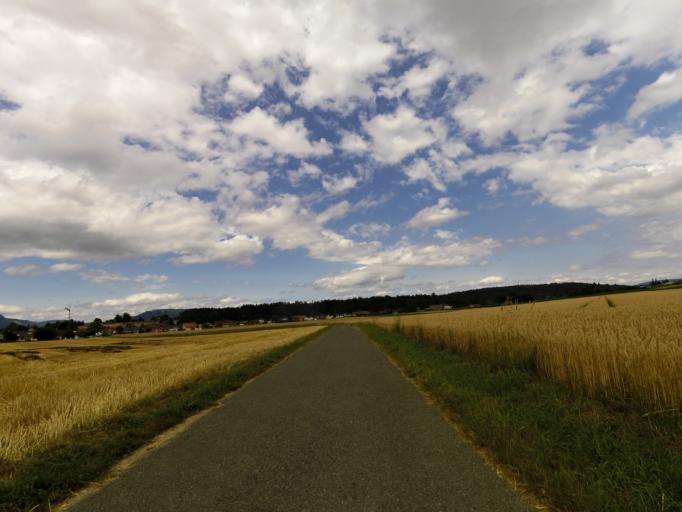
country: CH
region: Bern
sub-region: Oberaargau
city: Aarwangen
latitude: 47.2318
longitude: 7.7850
